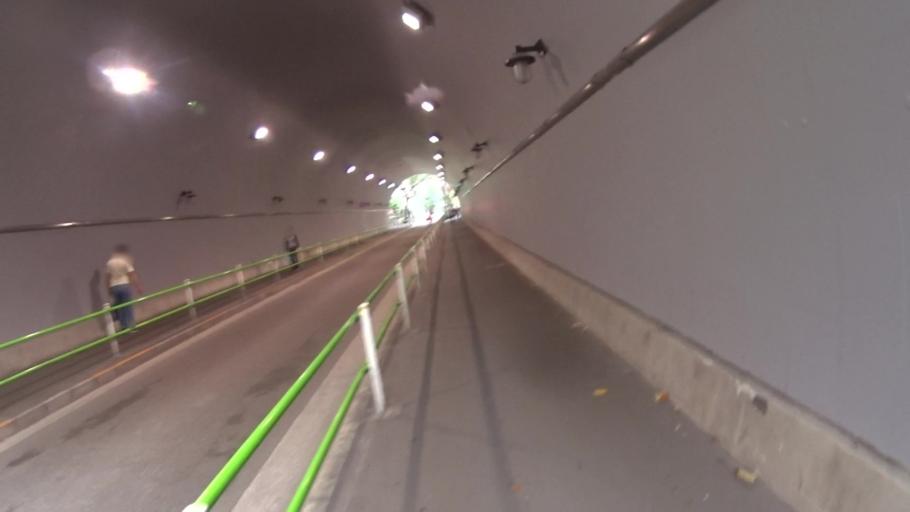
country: JP
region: Tokyo
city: Tokyo
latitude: 35.6641
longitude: 139.7491
